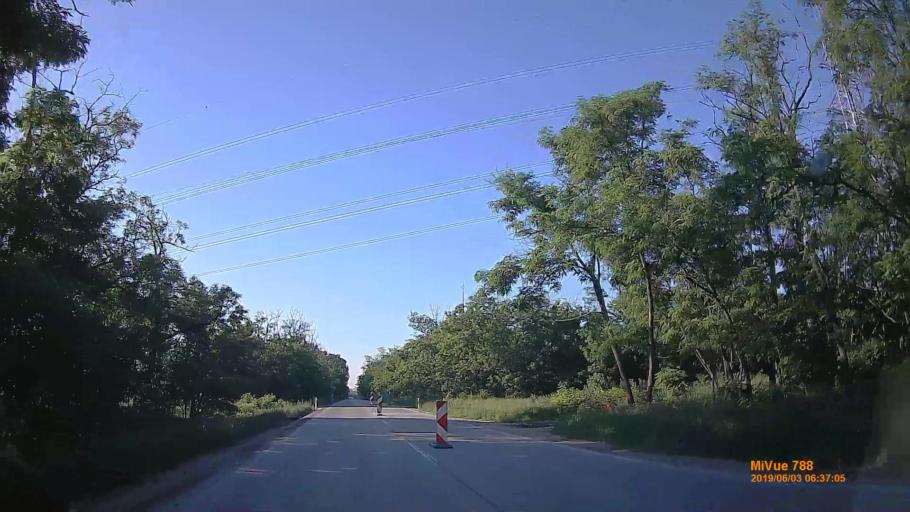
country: HU
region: Pest
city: Dunavarsany
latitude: 47.3037
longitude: 19.0853
